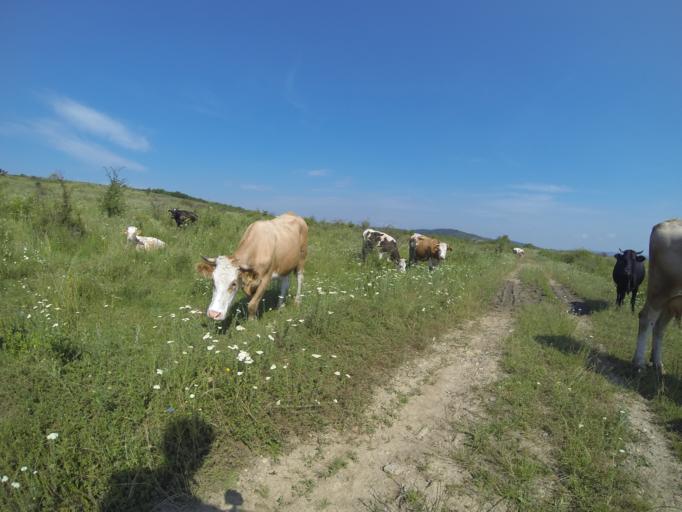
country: RO
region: Gorj
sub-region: Comuna Crusetu
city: Crusetu
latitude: 44.6111
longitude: 23.6687
